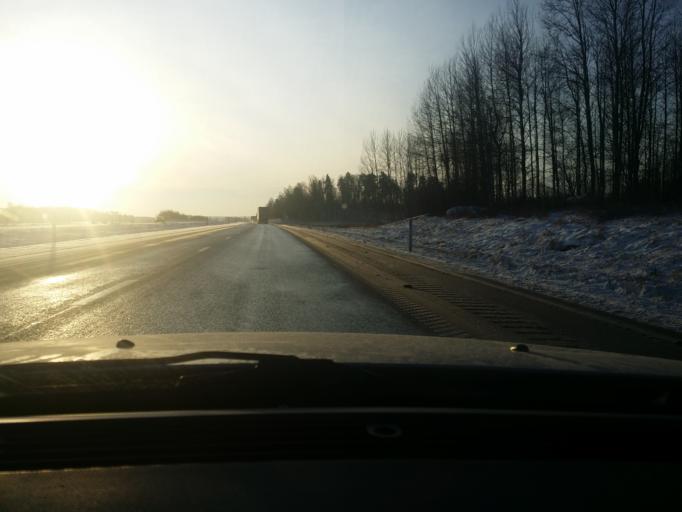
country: SE
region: Vaestmanland
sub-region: Arboga Kommun
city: Arboga
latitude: 59.4526
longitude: 15.8976
